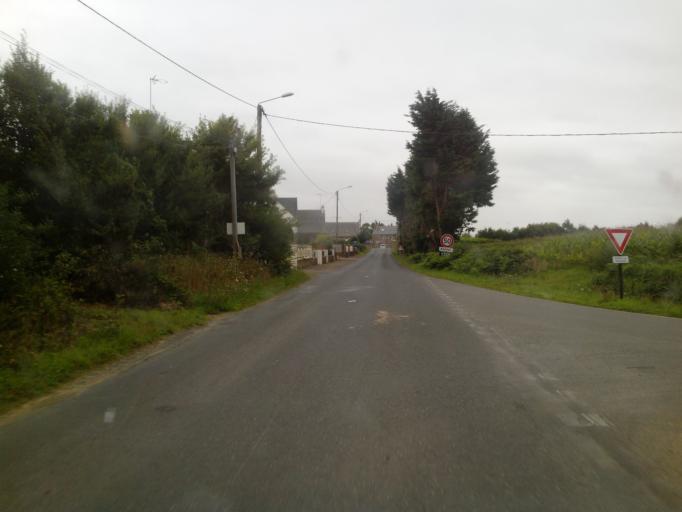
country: FR
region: Brittany
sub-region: Departement des Cotes-d'Armor
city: Pleubian
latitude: 48.8352
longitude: -3.1051
